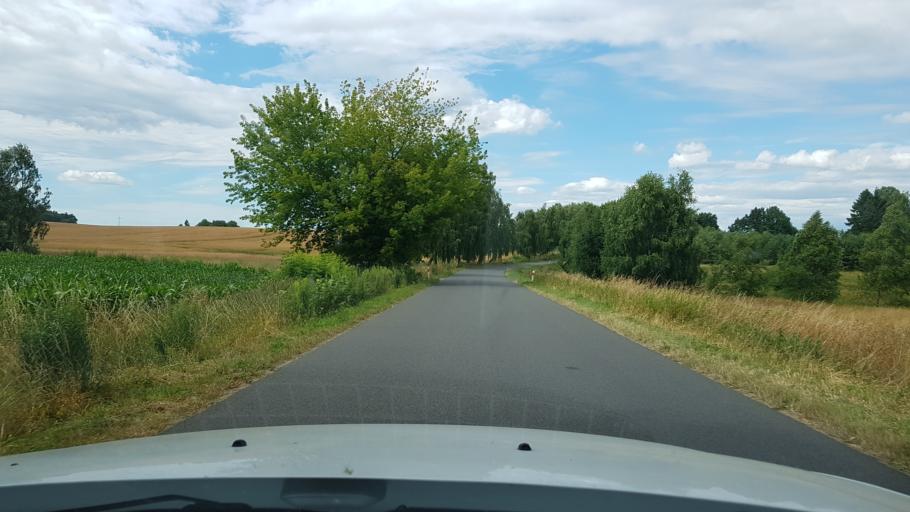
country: PL
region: West Pomeranian Voivodeship
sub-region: Powiat drawski
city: Kalisz Pomorski
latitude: 53.3138
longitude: 15.9201
